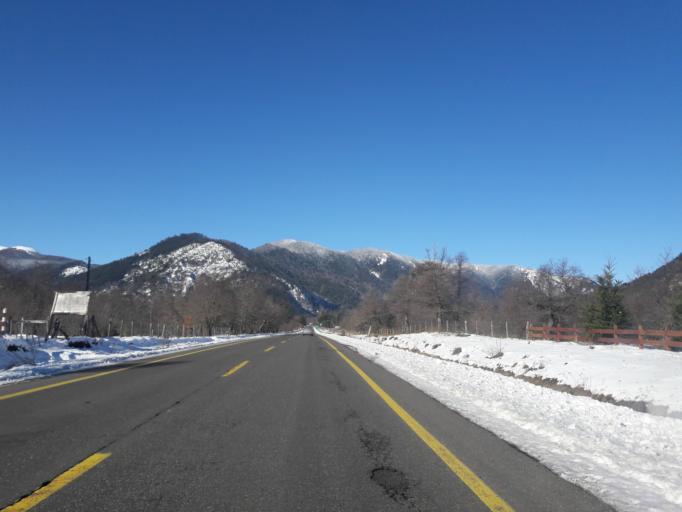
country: CL
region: Araucania
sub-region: Provincia de Cautin
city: Vilcun
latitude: -38.4756
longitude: -71.5485
